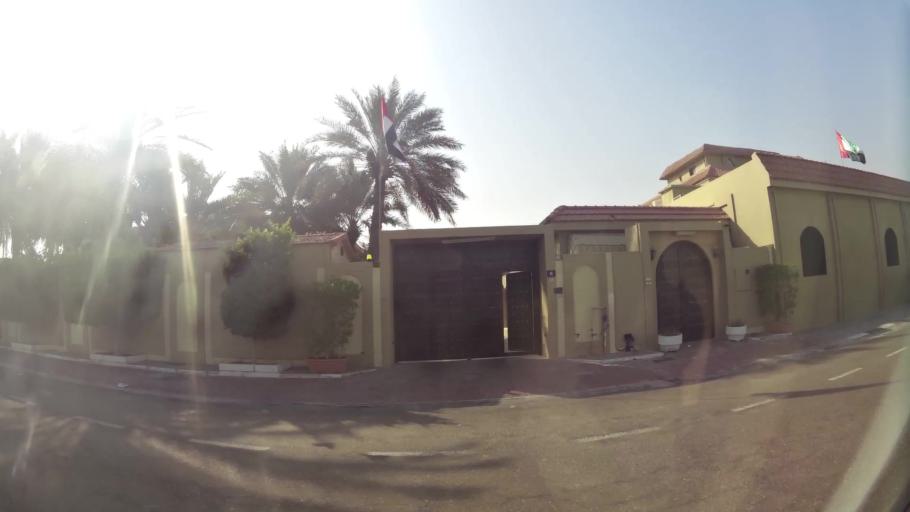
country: AE
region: Ash Shariqah
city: Sharjah
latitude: 25.3096
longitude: 55.3431
